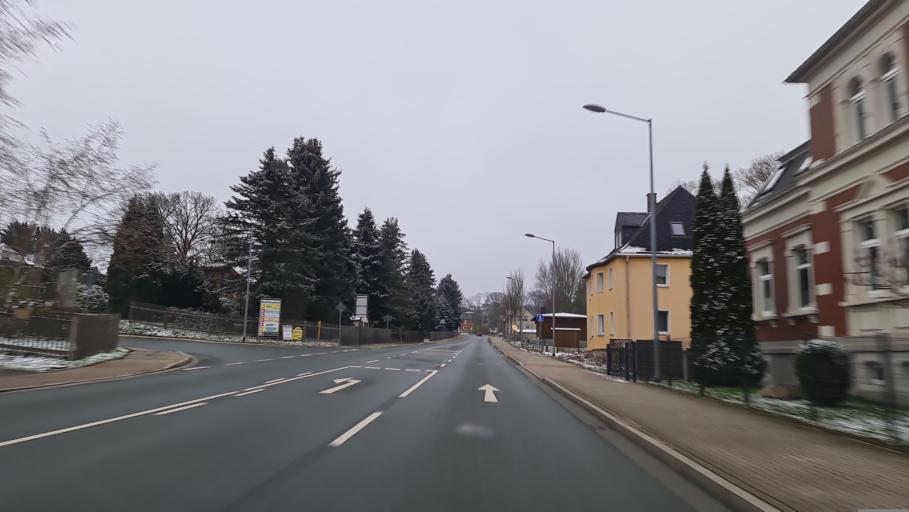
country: DE
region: Saxony
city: Markneukirchen
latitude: 50.3166
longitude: 12.3423
